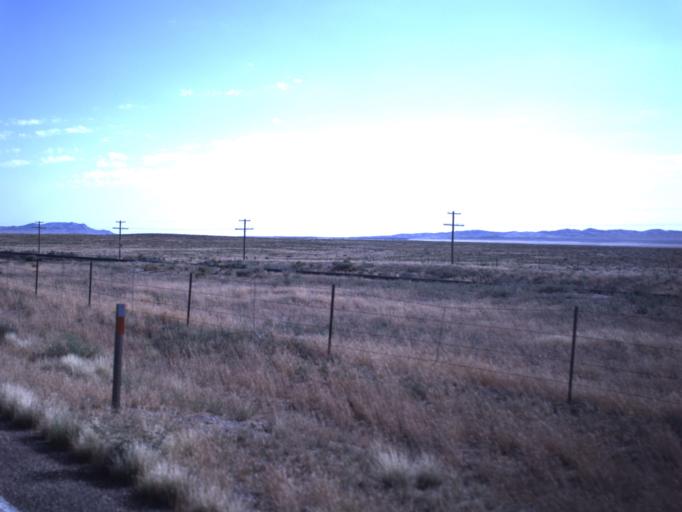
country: US
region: Utah
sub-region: Beaver County
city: Milford
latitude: 38.6657
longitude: -112.9810
